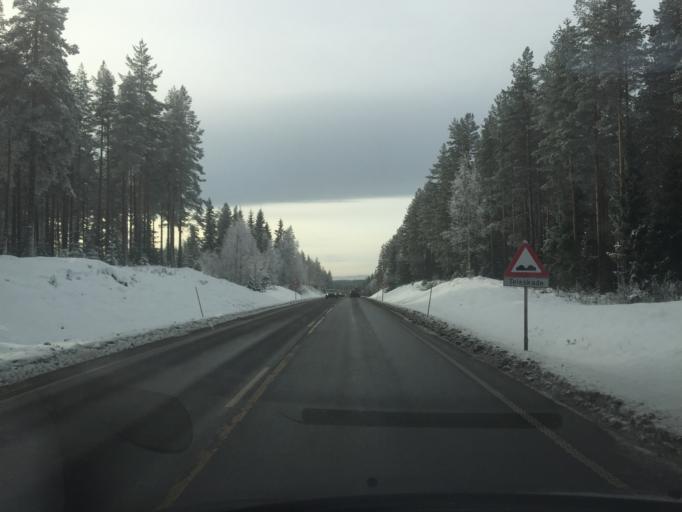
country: NO
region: Hedmark
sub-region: Elverum
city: Elverum
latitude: 60.9615
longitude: 11.7113
